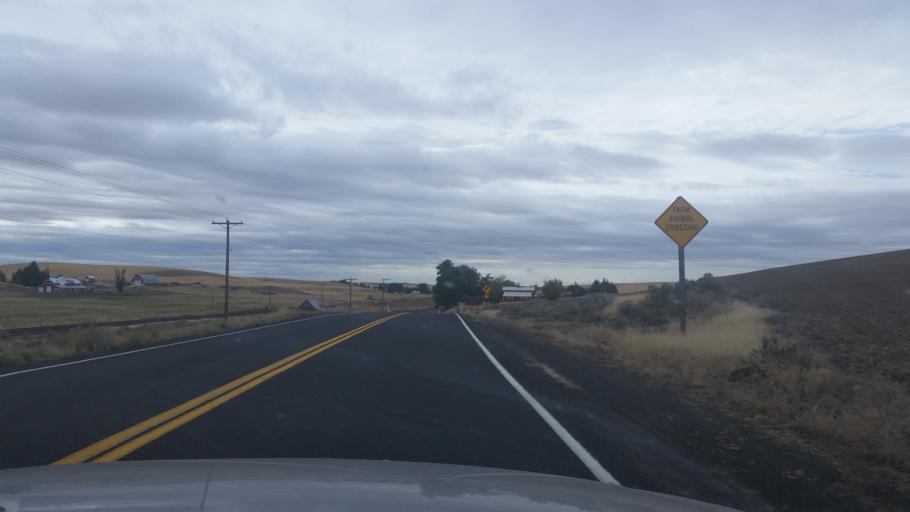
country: US
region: Washington
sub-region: Spokane County
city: Medical Lake
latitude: 47.5178
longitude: -117.9295
